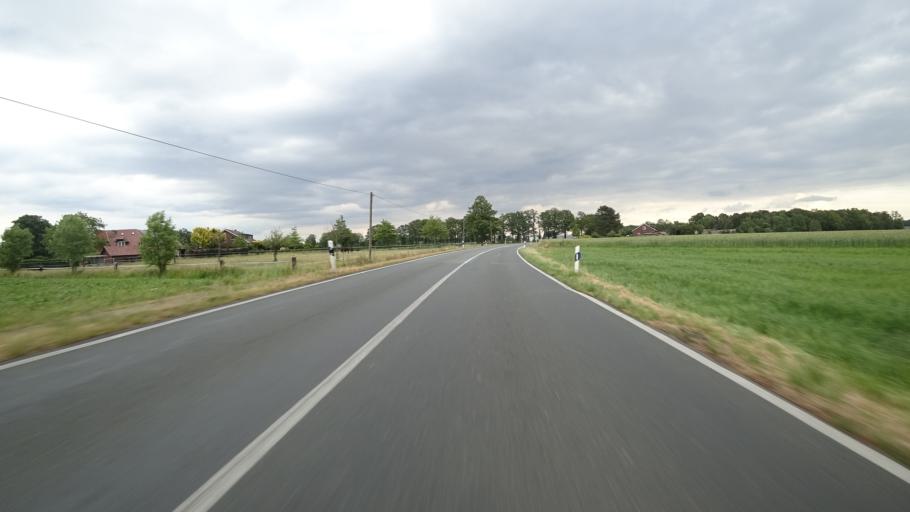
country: DE
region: North Rhine-Westphalia
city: Rietberg
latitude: 51.8397
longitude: 8.3913
